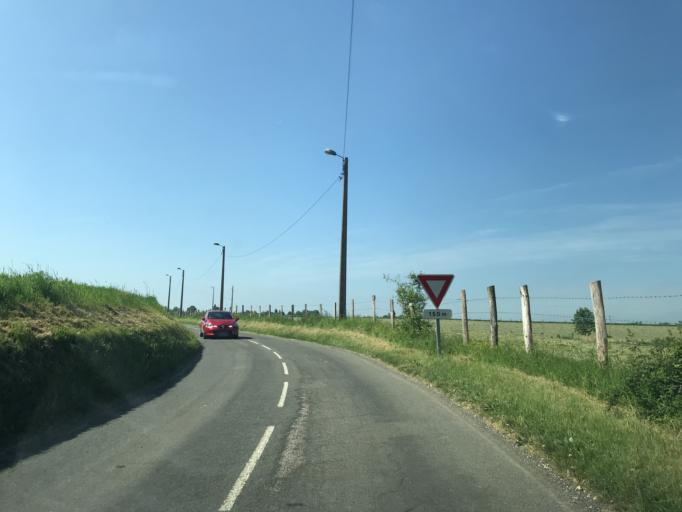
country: FR
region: Haute-Normandie
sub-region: Departement de la Seine-Maritime
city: Les Authieux-sur-le-Port-Saint-Ouen
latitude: 49.3510
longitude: 1.1471
